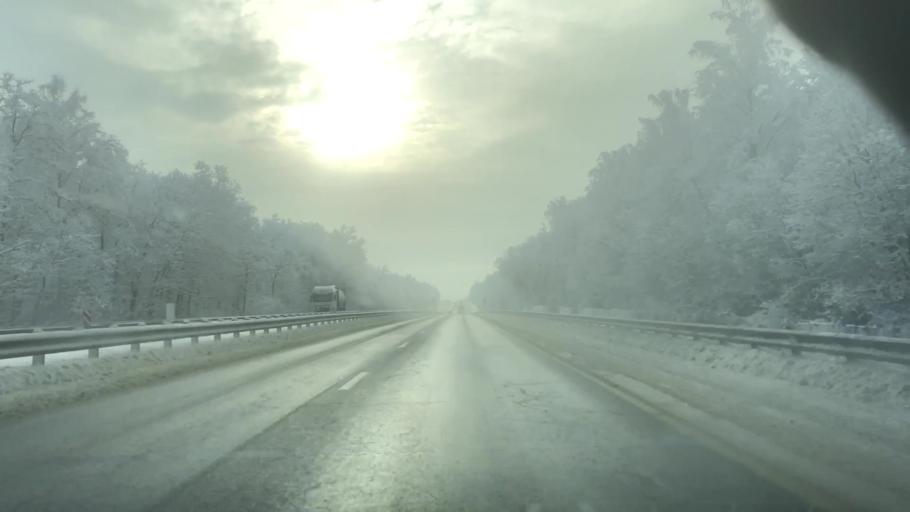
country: RU
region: Tula
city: Venev
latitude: 54.3662
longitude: 38.1547
